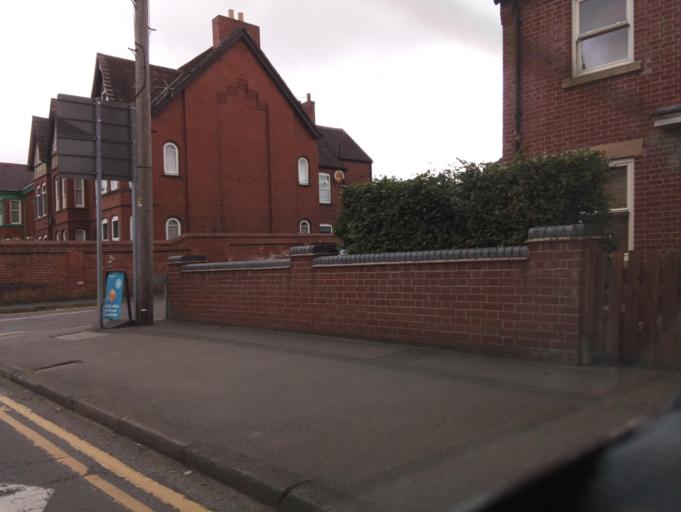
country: GB
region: England
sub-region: Leicestershire
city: Coalville
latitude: 52.7210
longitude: -1.3609
